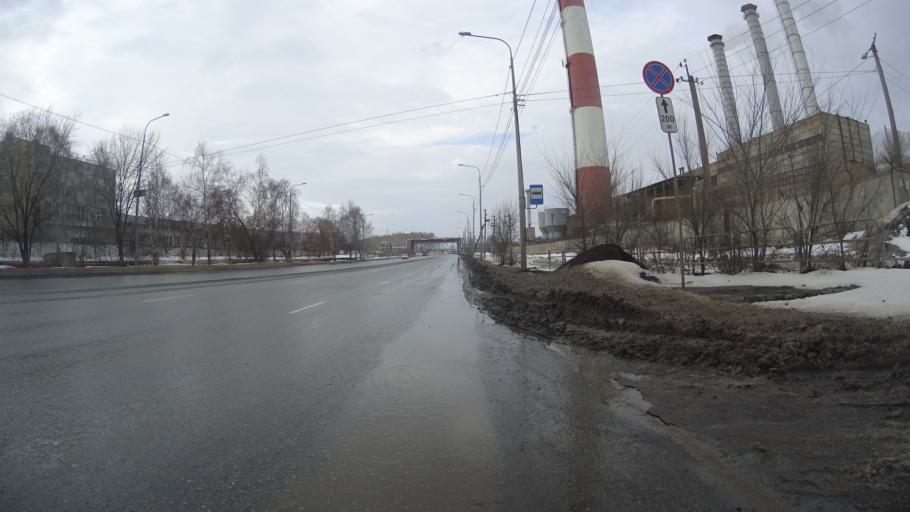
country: RU
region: Chelyabinsk
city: Roshchino
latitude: 55.2061
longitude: 61.3209
